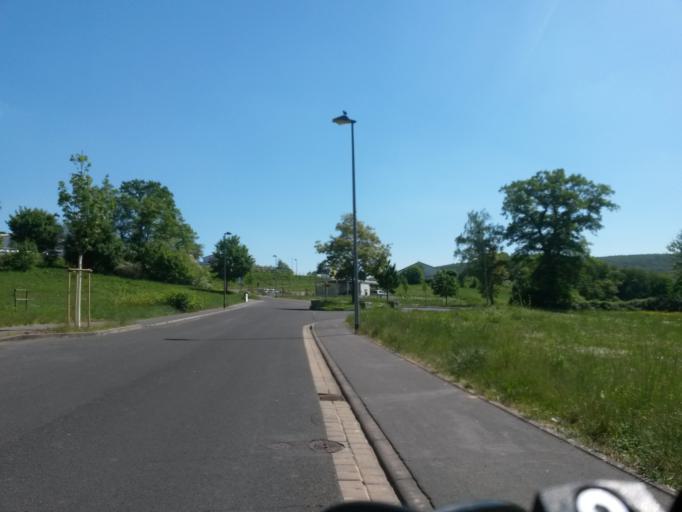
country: DE
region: Bavaria
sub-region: Regierungsbezirk Unterfranken
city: Bad Kissingen
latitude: 50.1820
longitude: 10.0775
